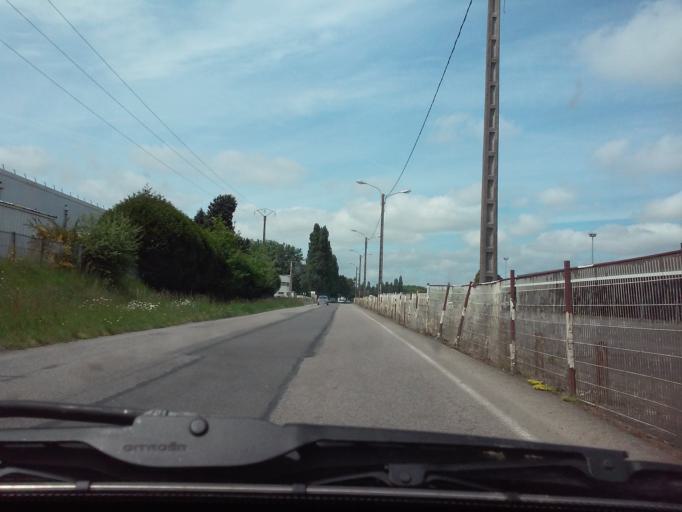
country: FR
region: Brittany
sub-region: Departement d'Ille-et-Vilaine
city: Beauce
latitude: 48.3343
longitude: -1.1703
